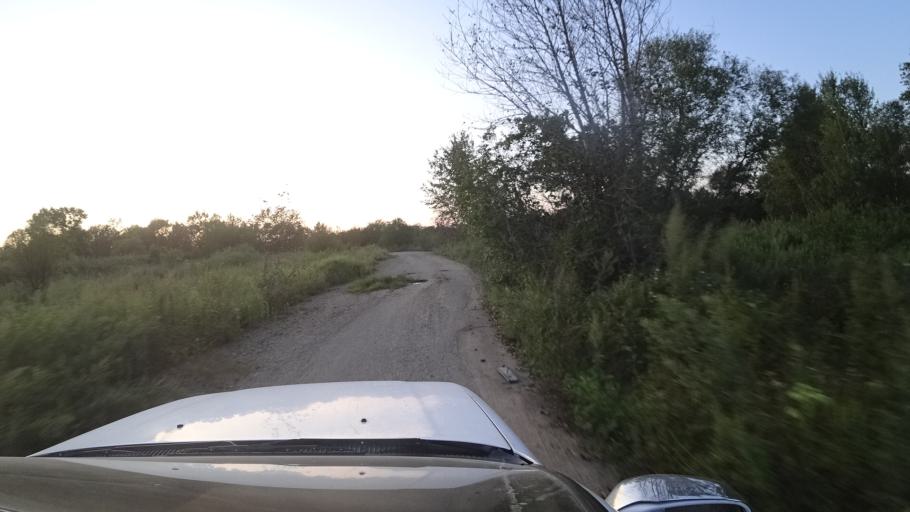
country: RU
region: Primorskiy
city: Dal'nerechensk
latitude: 45.9495
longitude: 133.7609
